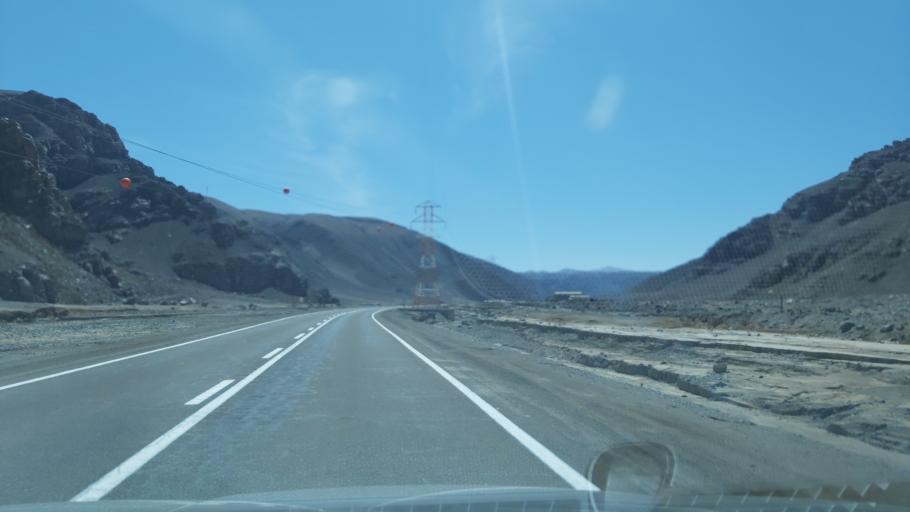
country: CL
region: Atacama
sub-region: Provincia de Chanaral
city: Diego de Almagro
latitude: -26.3370
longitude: -69.8325
